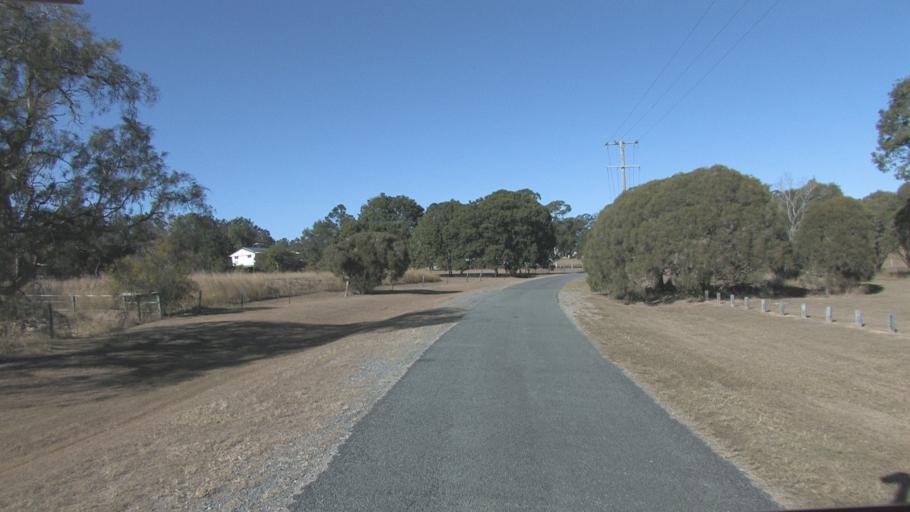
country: AU
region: Queensland
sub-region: Logan
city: Cedar Vale
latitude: -27.8482
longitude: 153.0088
